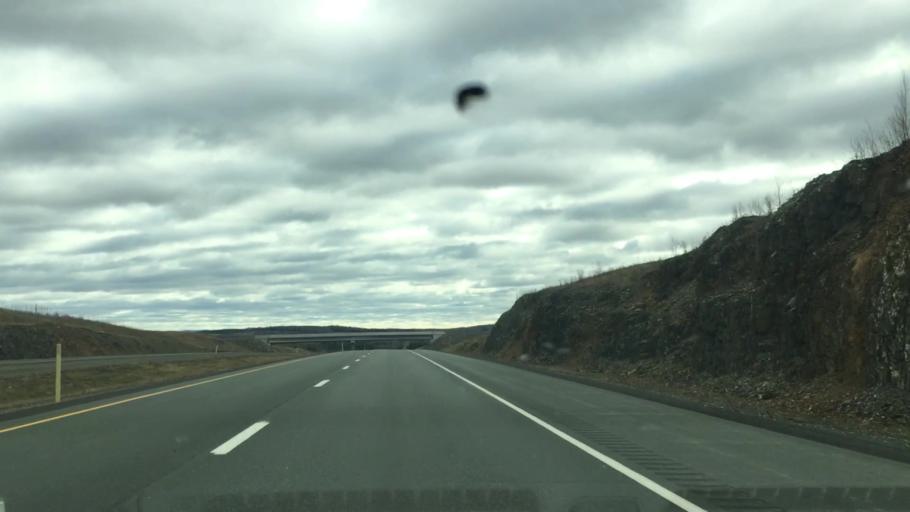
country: CA
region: New Brunswick
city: Florenceville-Bristol
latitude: 46.5494
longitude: -67.7312
